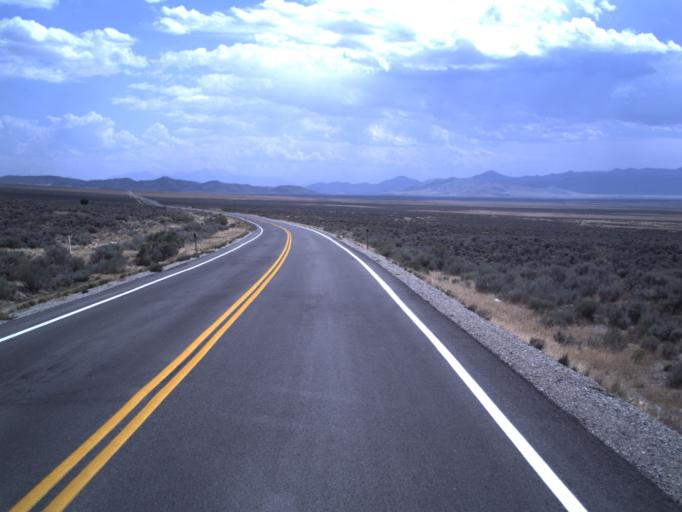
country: US
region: Utah
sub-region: Tooele County
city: Tooele
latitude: 40.2919
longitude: -112.2717
